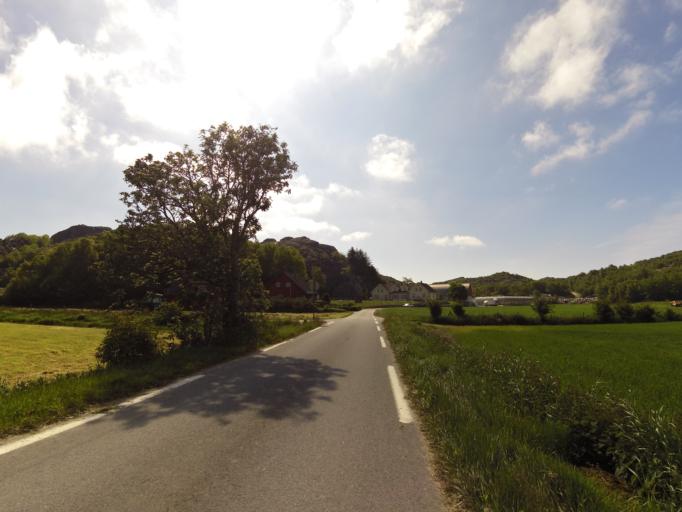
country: NO
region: Rogaland
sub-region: Ha
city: Vigrestad
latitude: 58.5168
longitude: 5.8218
